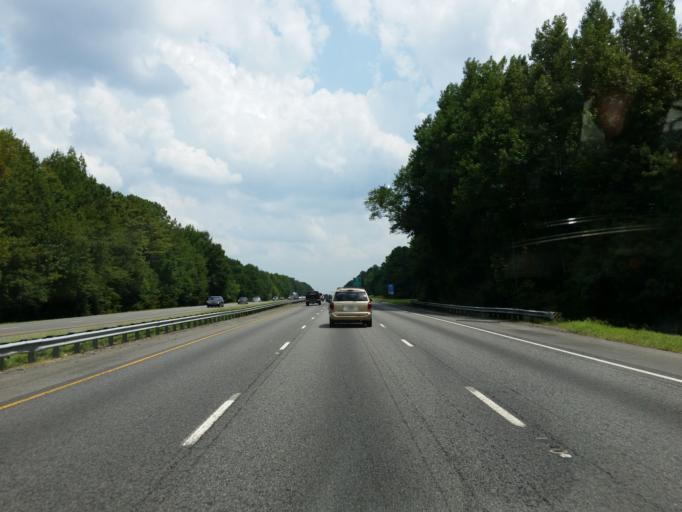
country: US
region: Georgia
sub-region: Butts County
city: Jackson
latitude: 33.2199
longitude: -84.0707
